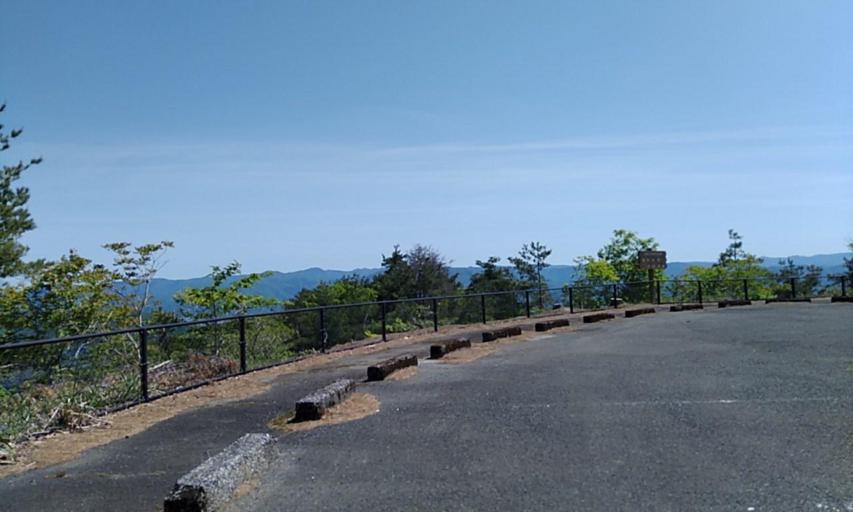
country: JP
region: Fukui
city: Obama
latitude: 35.5483
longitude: 135.7446
